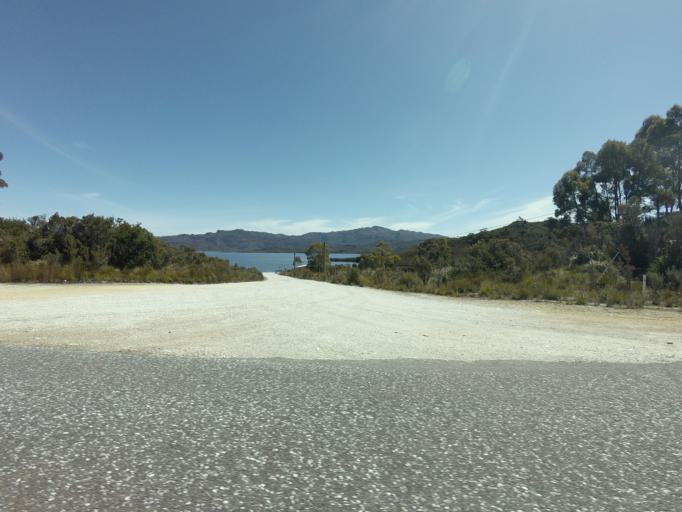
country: AU
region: Tasmania
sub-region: West Coast
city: Queenstown
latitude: -42.7866
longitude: 146.0622
